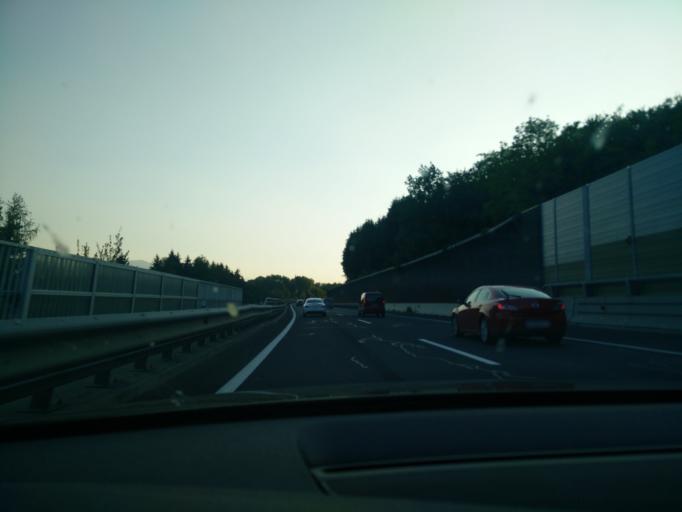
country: AT
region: Carinthia
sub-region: Politischer Bezirk Villach Land
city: Velden am Woerthersee
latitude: 46.6240
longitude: 14.0502
